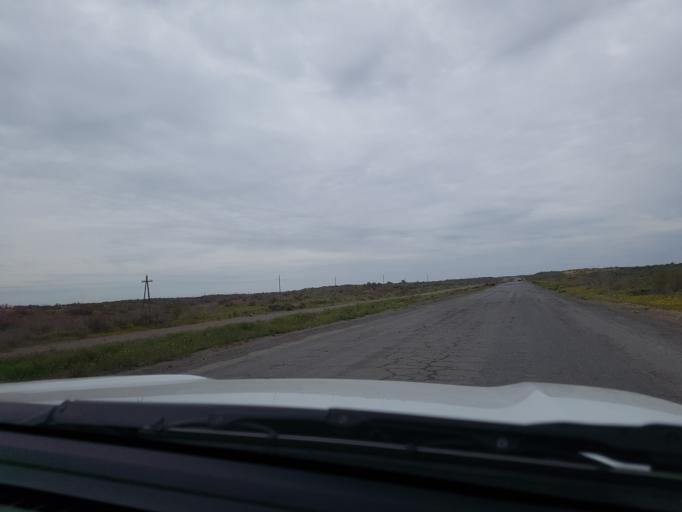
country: TM
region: Mary
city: Bayramaly
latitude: 37.9041
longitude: 62.6190
